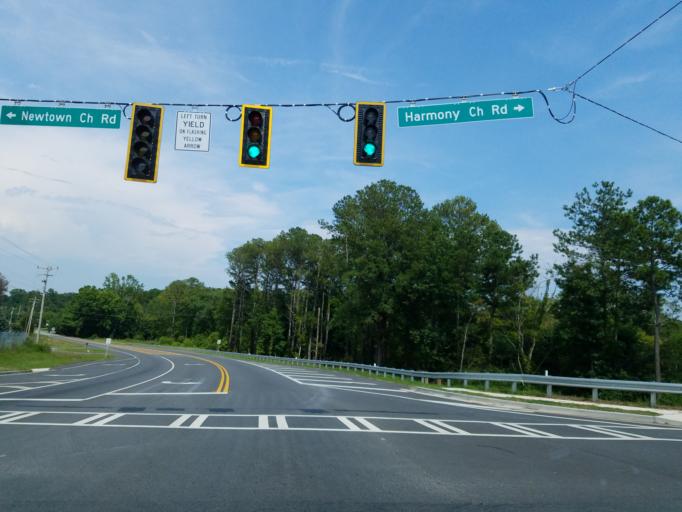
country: US
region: Georgia
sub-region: Gordon County
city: Calhoun
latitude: 34.5111
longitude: -84.9146
